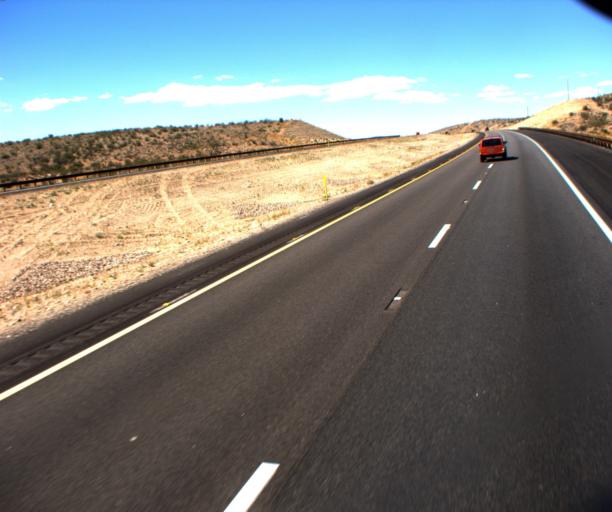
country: US
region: Arizona
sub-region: Mohave County
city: Kingman
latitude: 34.9944
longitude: -113.6647
